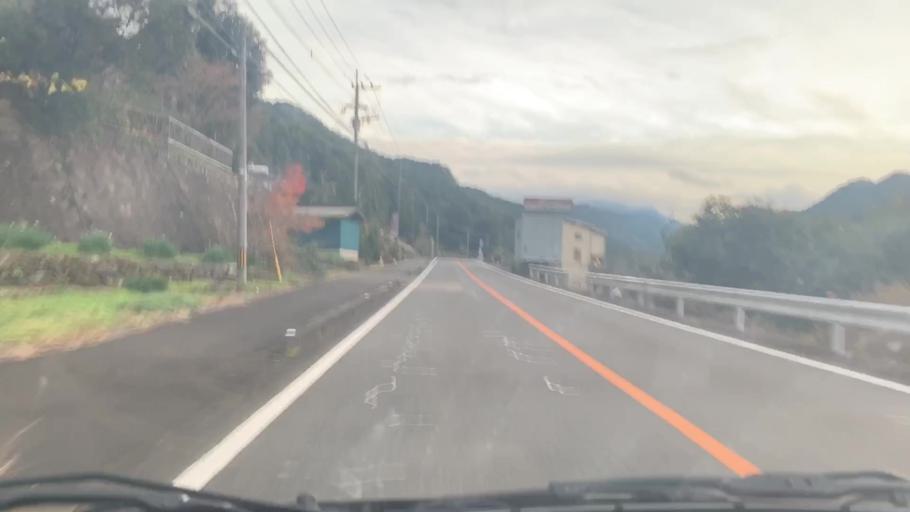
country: JP
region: Saga Prefecture
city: Kashima
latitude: 33.0708
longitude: 130.0694
